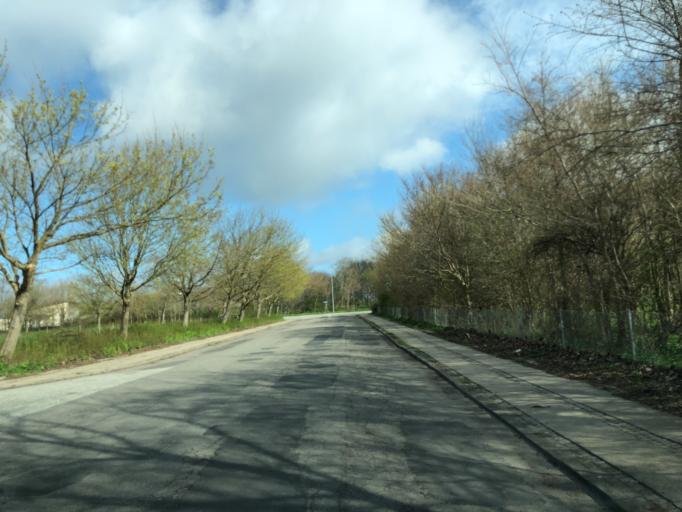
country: DK
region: North Denmark
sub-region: Alborg Kommune
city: Aalborg
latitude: 57.0536
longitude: 9.8838
